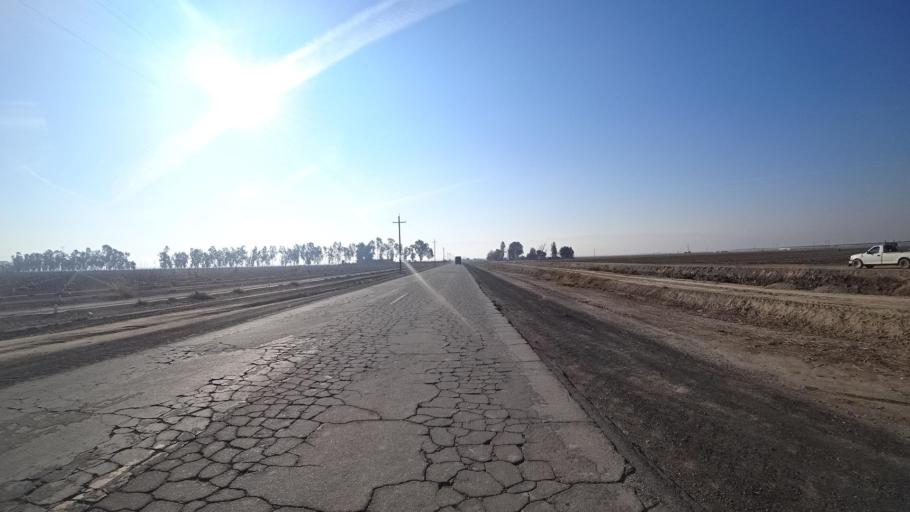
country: US
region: California
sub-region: Kern County
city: Weedpatch
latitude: 35.1904
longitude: -118.9677
